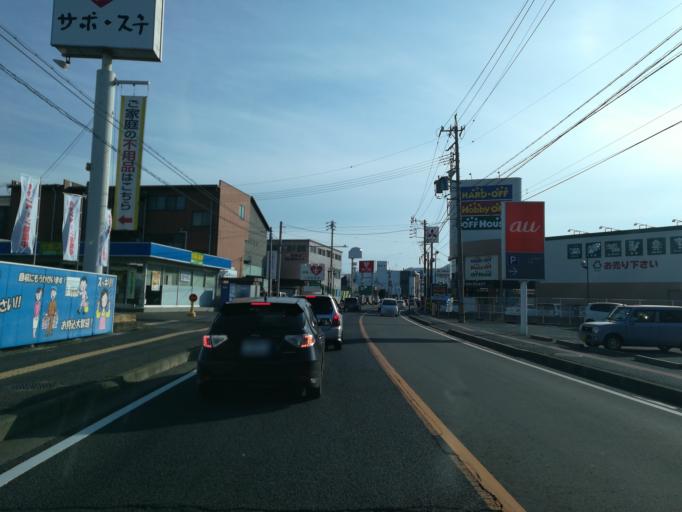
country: JP
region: Nagano
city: Ueda
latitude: 36.3960
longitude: 138.2659
